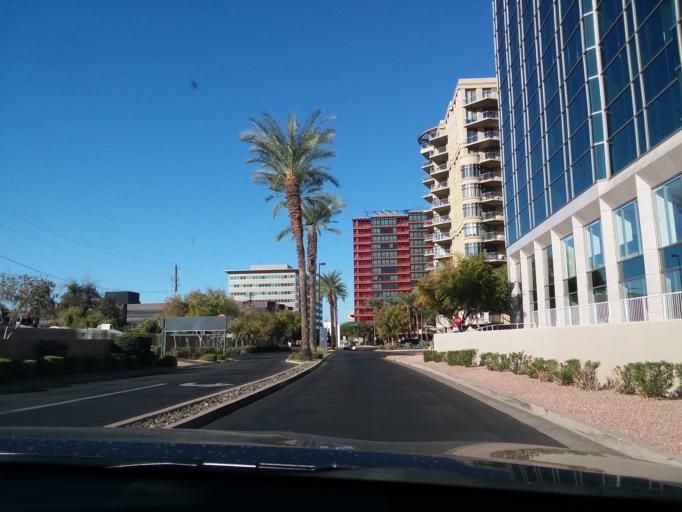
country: US
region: Arizona
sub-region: Maricopa County
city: Phoenix
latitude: 33.5078
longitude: -112.0285
